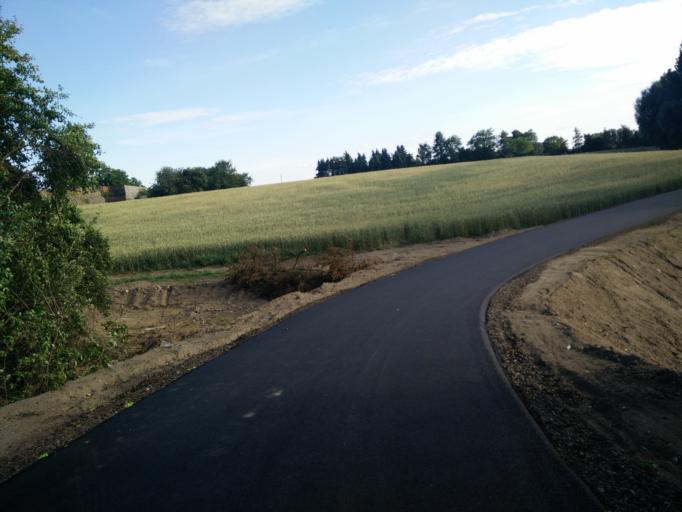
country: PL
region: Greater Poland Voivodeship
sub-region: Powiat sredzki
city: Sroda Wielkopolska
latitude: 52.2450
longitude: 17.2980
